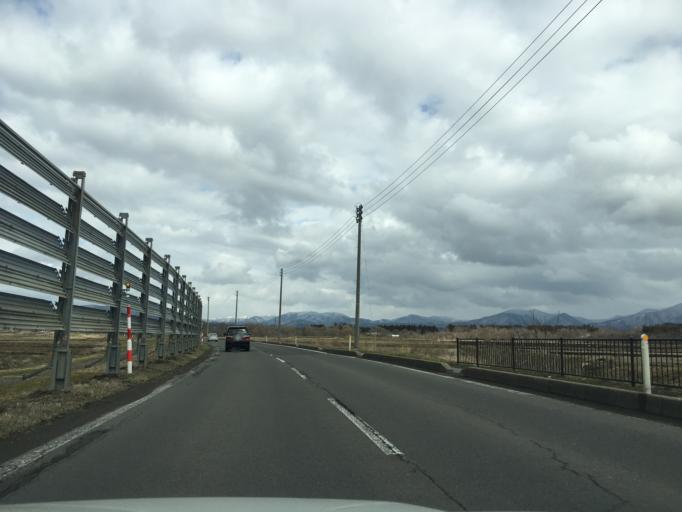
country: JP
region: Akita
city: Hanawa
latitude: 40.2491
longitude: 140.7562
